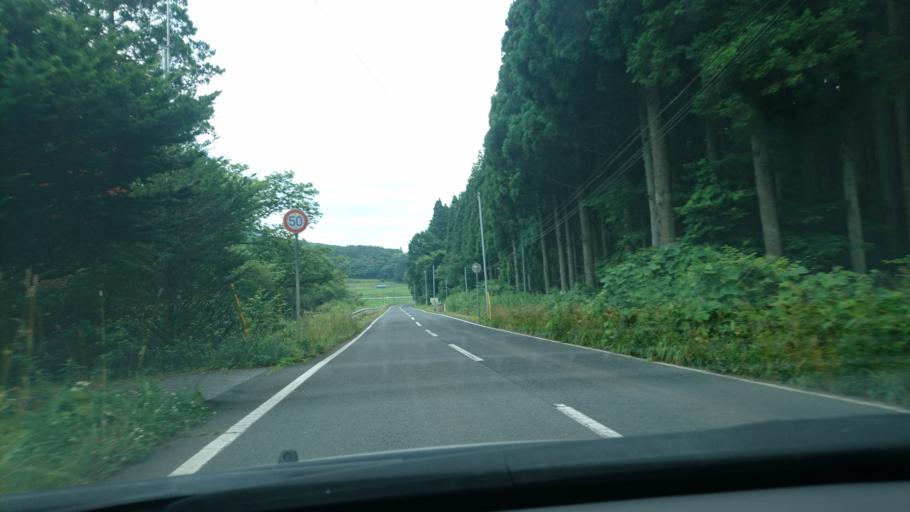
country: JP
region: Iwate
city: Ichinoseki
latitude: 38.8814
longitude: 141.4258
